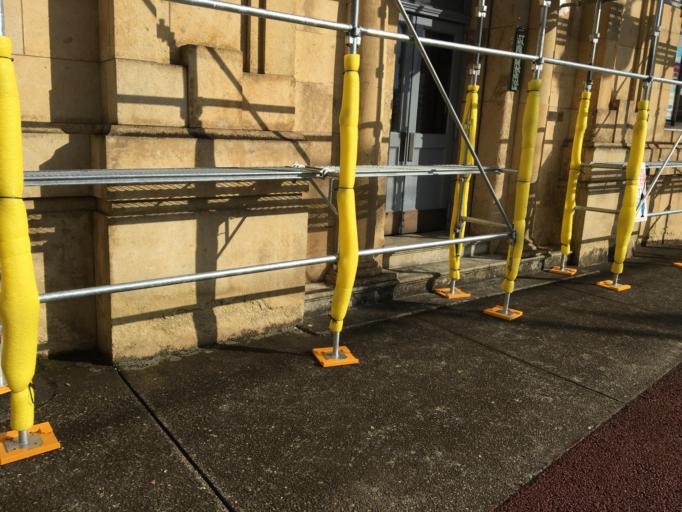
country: JP
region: Chiba
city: Noda
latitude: 35.9441
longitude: 139.8628
